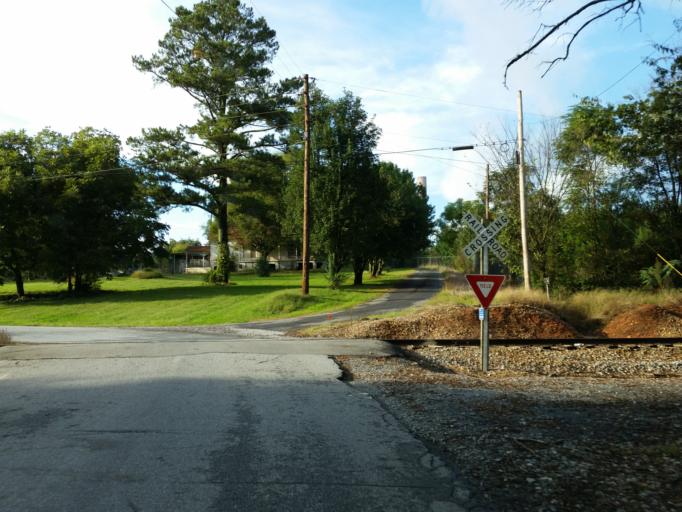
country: US
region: Georgia
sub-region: Bartow County
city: Euharlee
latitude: 34.1127
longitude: -84.9188
